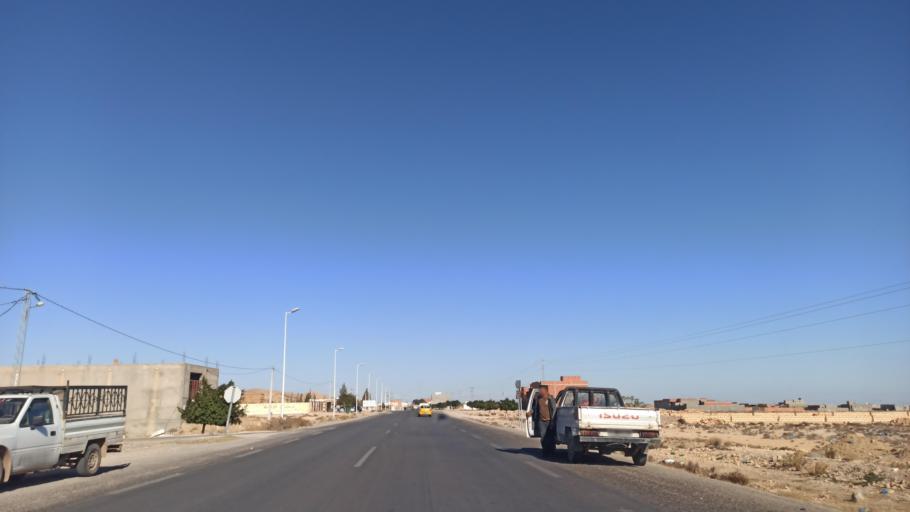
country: TN
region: Sidi Bu Zayd
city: Bi'r al Hufayy
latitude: 34.9130
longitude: 9.1828
